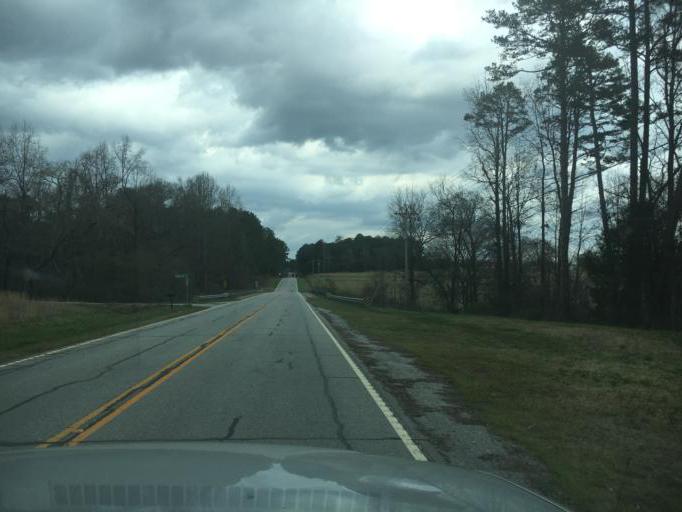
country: US
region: South Carolina
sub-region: Oconee County
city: Westminster
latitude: 34.7057
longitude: -83.0736
